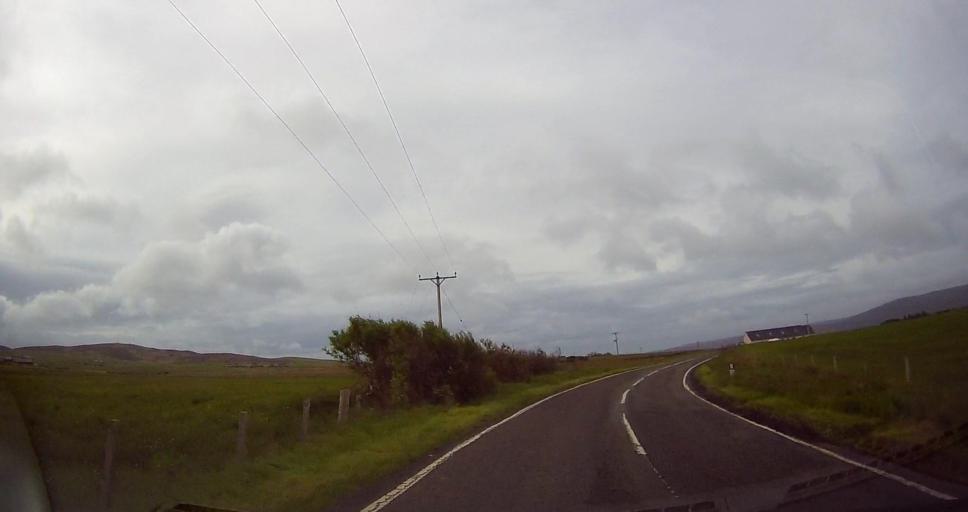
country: GB
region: Scotland
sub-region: Orkney Islands
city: Stromness
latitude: 58.9405
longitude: -3.2138
